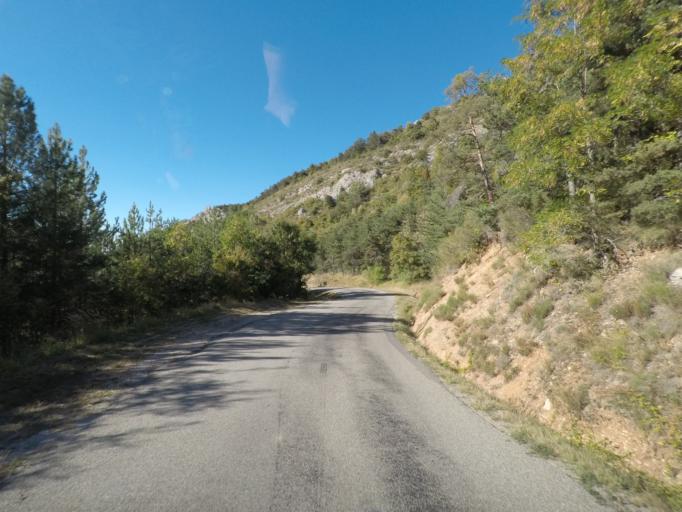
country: FR
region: Provence-Alpes-Cote d'Azur
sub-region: Departement des Hautes-Alpes
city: Serres
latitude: 44.4382
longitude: 5.5743
